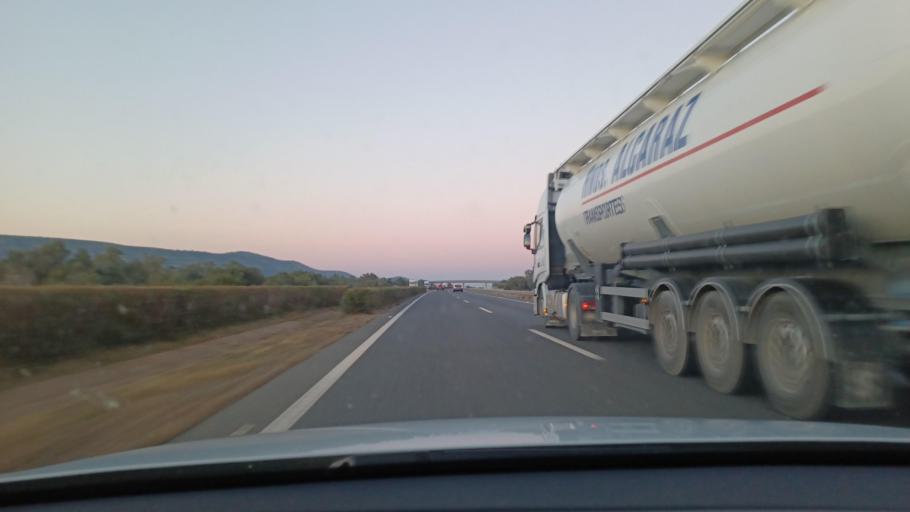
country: ES
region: Catalonia
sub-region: Provincia de Tarragona
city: Ulldecona
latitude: 40.6089
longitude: 0.4759
